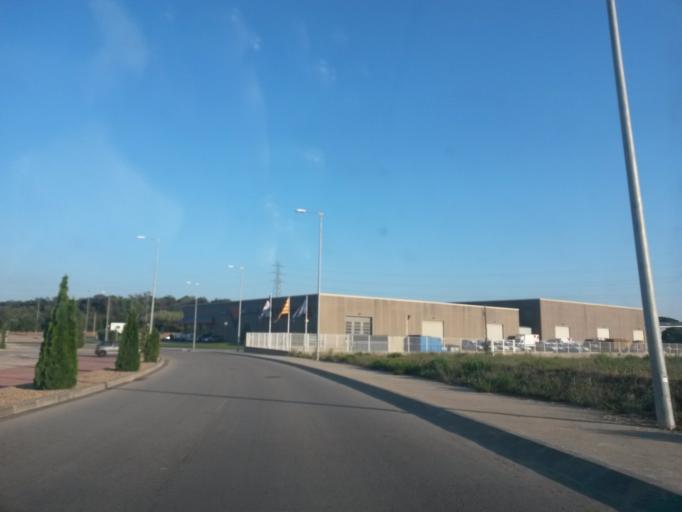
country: ES
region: Catalonia
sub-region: Provincia de Girona
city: Fornells de la Selva
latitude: 41.9415
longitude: 2.8011
